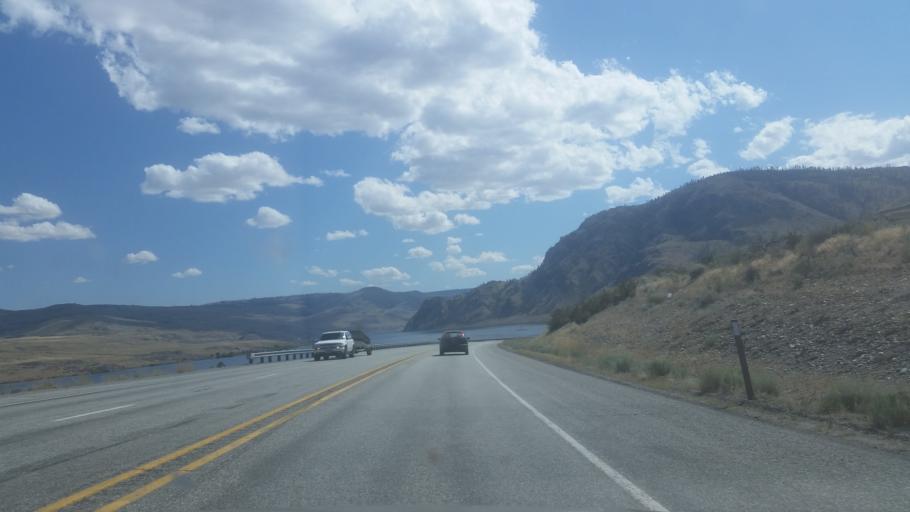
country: US
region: Washington
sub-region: Okanogan County
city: Brewster
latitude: 47.9983
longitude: -119.8838
